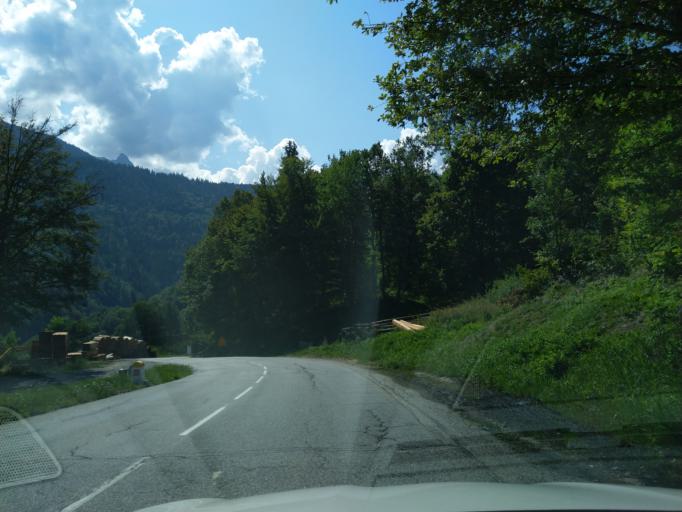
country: FR
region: Rhone-Alpes
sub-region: Departement de la Savoie
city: Les Allues
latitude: 45.4404
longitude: 6.5574
